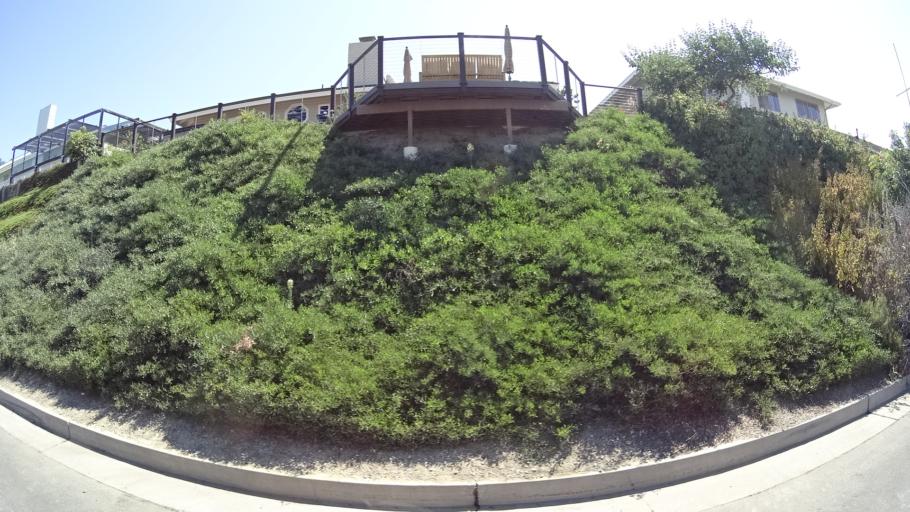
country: US
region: California
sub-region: Orange County
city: San Clemente
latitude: 33.4442
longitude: -117.6356
